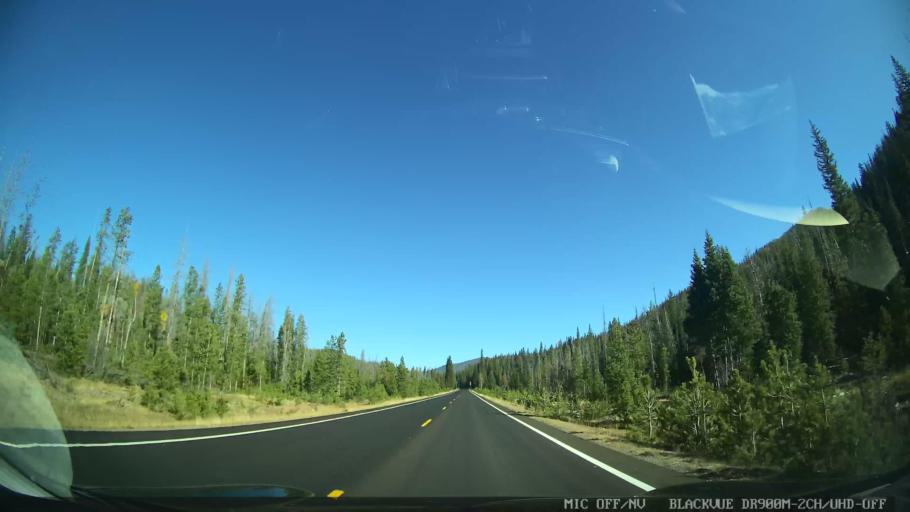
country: US
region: Colorado
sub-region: Grand County
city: Granby
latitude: 40.2929
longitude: -105.8432
